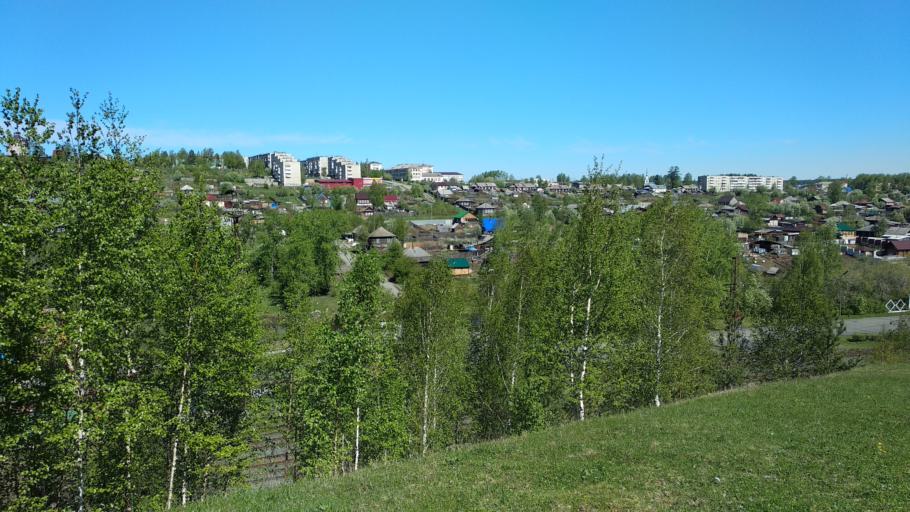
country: RU
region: Sverdlovsk
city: Karpinsk
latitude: 59.7510
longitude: 60.0177
